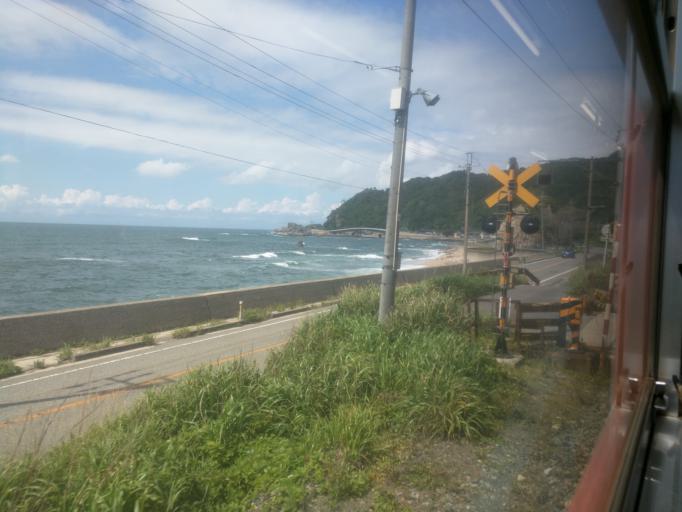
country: JP
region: Niigata
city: Murakami
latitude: 38.4290
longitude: 139.4796
